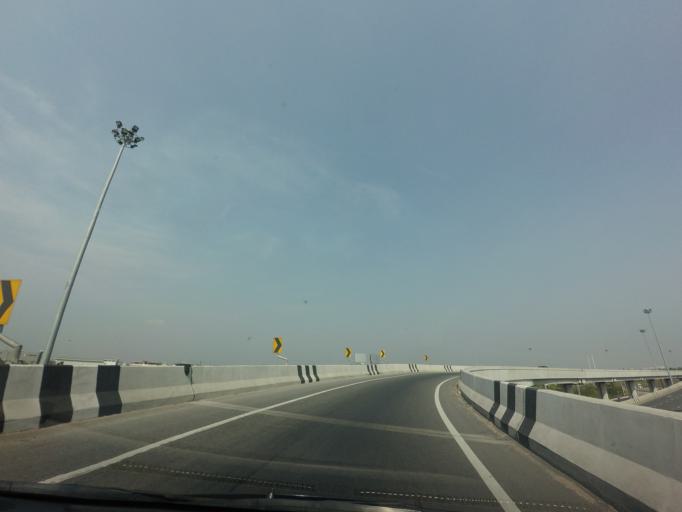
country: TH
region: Bangkok
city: Lat Krabang
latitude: 13.7559
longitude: 100.7441
